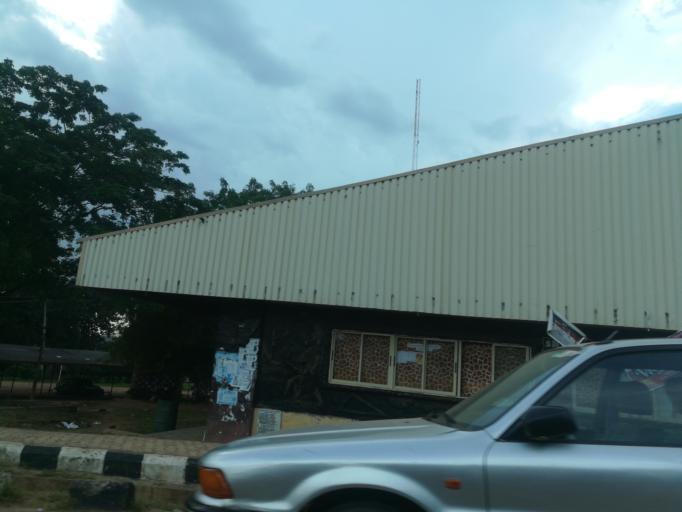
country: NG
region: Oyo
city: Ibadan
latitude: 7.4290
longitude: 3.8932
